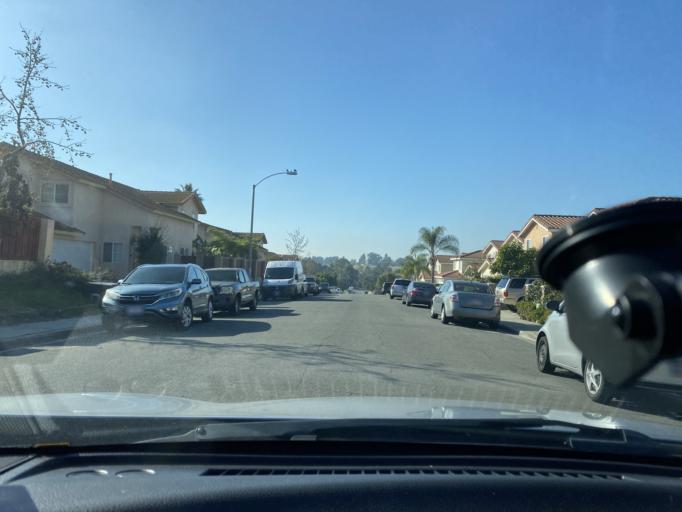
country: US
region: California
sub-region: San Diego County
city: National City
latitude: 32.7060
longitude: -117.0901
